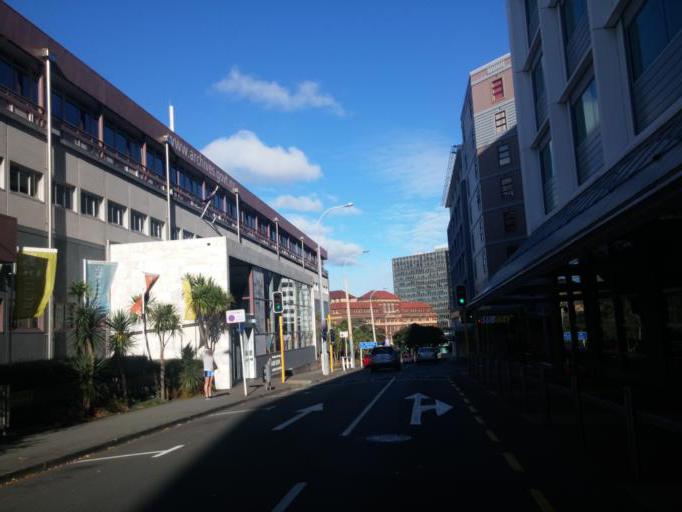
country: NZ
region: Wellington
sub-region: Wellington City
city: Wellington
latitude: -41.2767
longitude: 174.7798
